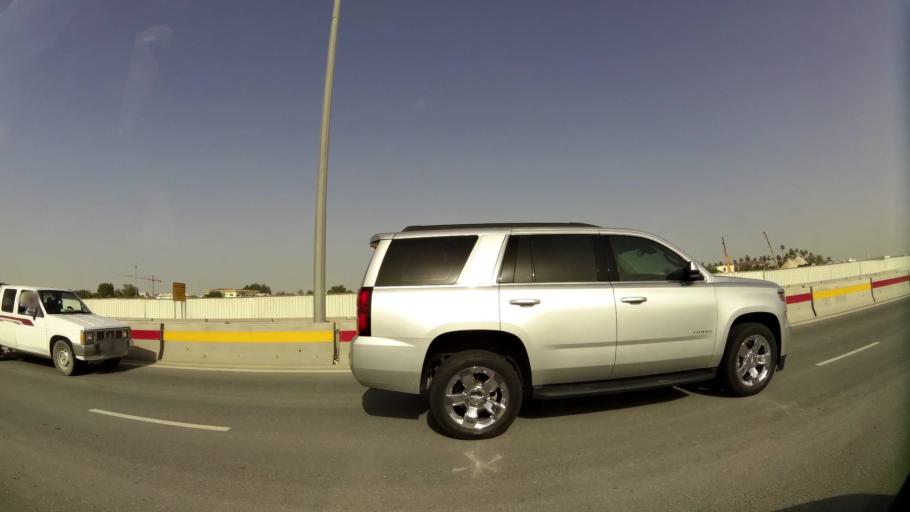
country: QA
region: Baladiyat ar Rayyan
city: Ar Rayyan
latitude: 25.3234
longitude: 51.4483
